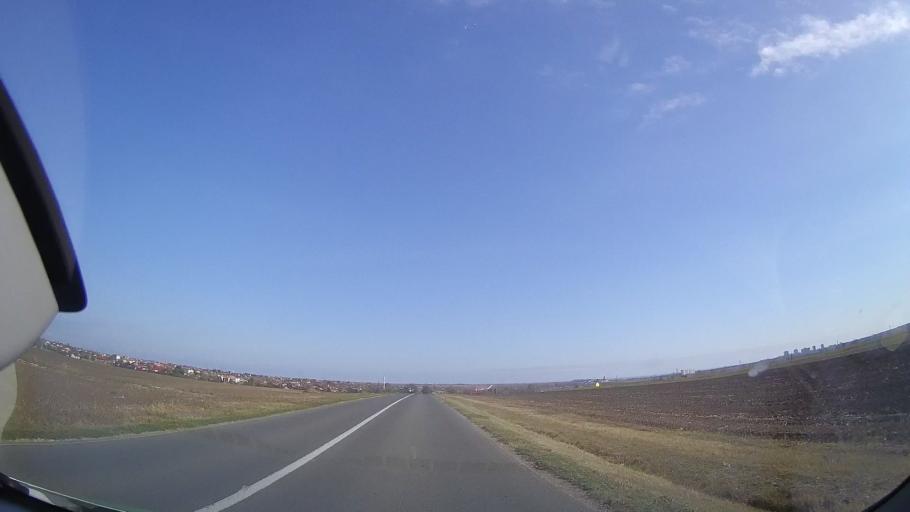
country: RO
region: Constanta
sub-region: Comuna Douazeci si Trei August
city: Douazeci si Trei August
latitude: 43.9138
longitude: 28.5720
